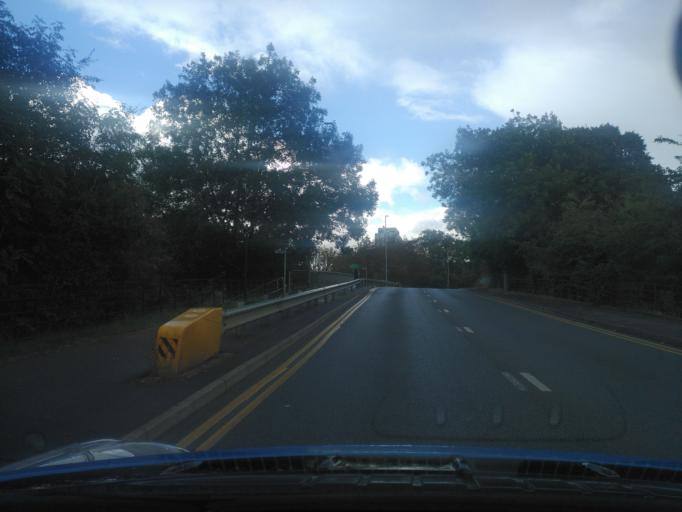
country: GB
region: England
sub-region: Hertfordshire
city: Hemel Hempstead
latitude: 51.7438
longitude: -0.4825
